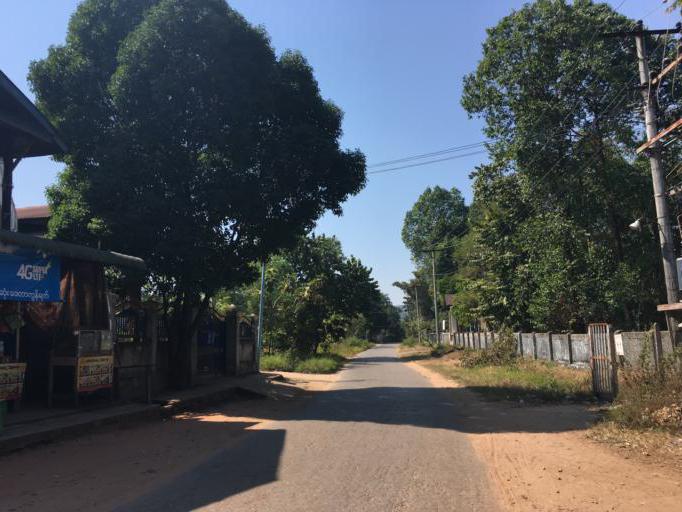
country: MM
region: Mon
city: Mawlamyine
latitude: 16.4347
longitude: 97.7013
